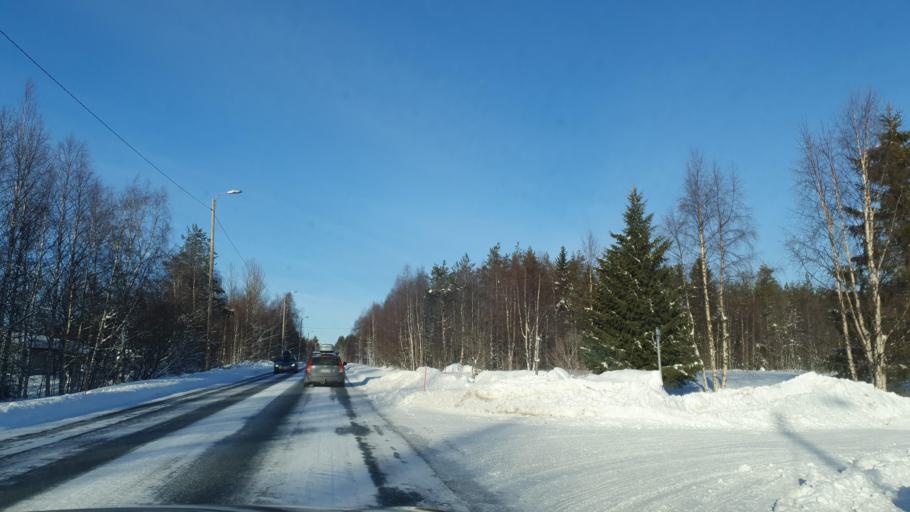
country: FI
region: Lapland
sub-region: Torniolaakso
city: Ylitornio
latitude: 66.1914
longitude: 23.8042
